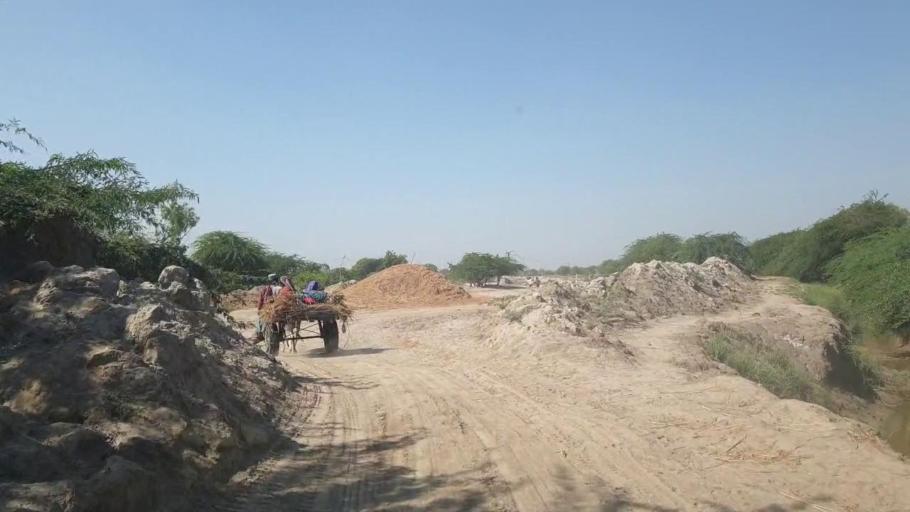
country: PK
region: Sindh
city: Talhar
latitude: 24.8060
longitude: 68.7939
